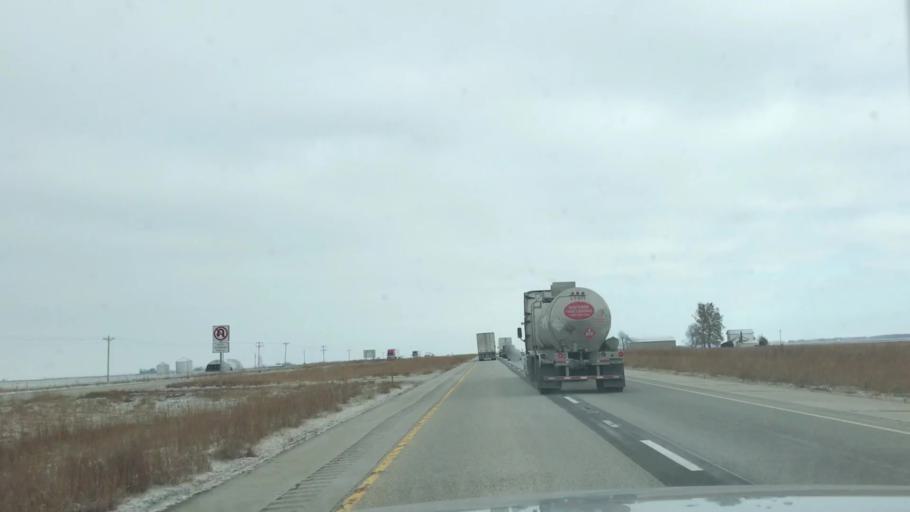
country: US
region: Illinois
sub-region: Sangamon County
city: Divernon
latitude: 39.4616
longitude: -89.6442
